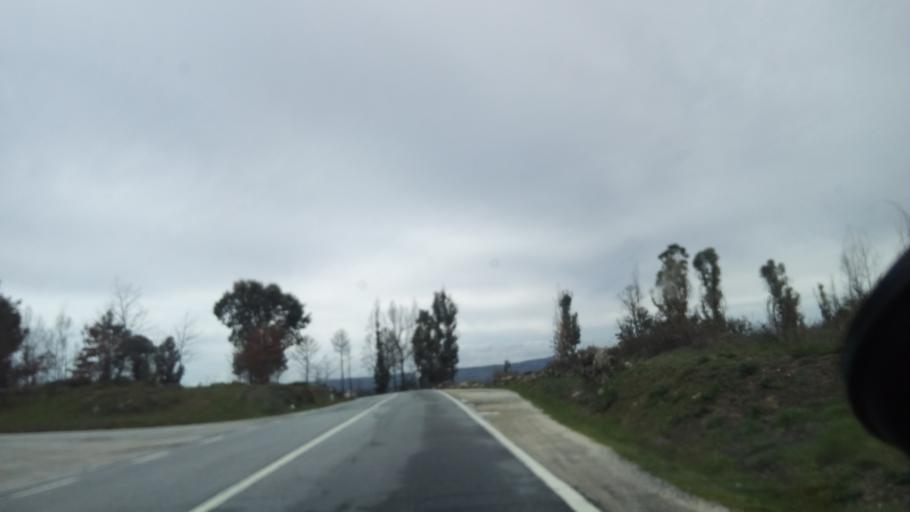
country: PT
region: Guarda
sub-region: Fornos de Algodres
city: Fornos de Algodres
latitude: 40.5232
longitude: -7.5985
